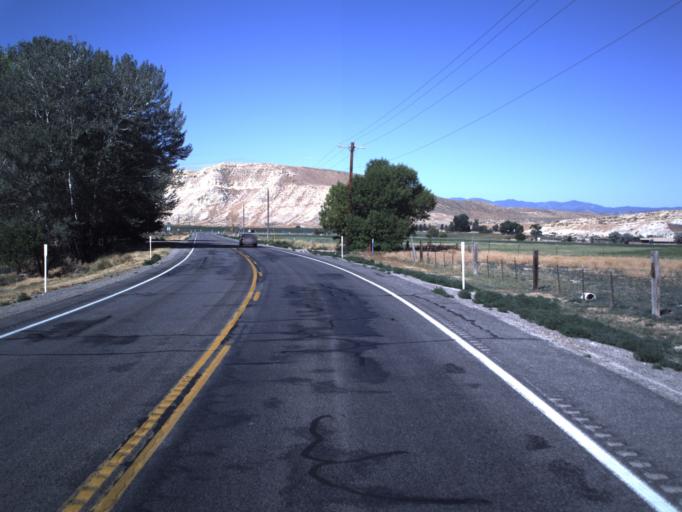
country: US
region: Utah
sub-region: Sanpete County
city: Gunnison
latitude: 39.1586
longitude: -111.7569
